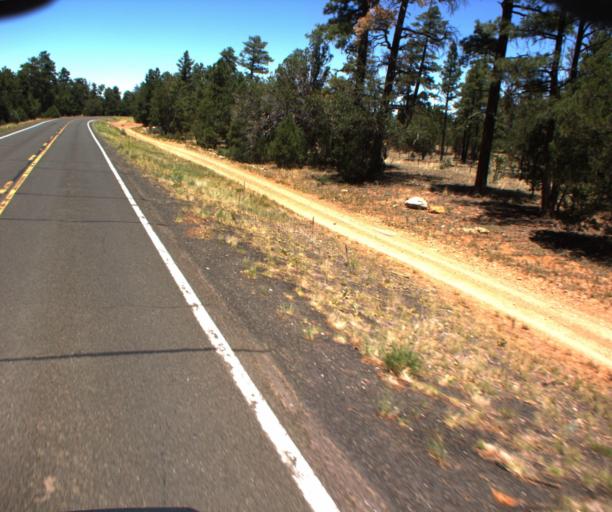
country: US
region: Arizona
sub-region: Gila County
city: Star Valley
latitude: 34.6558
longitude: -111.1091
